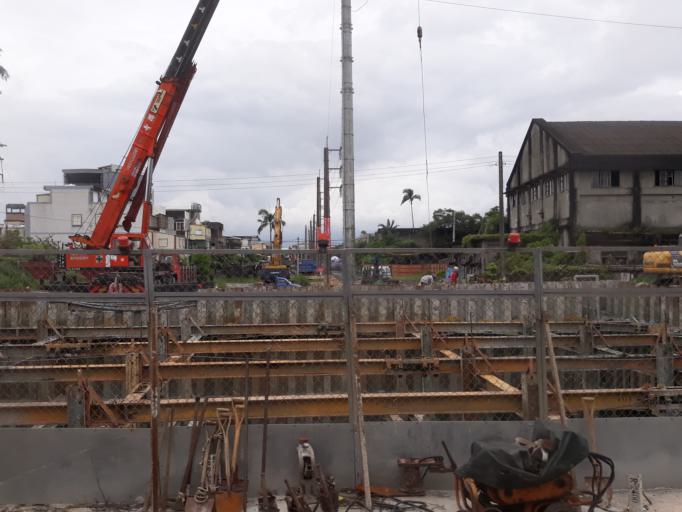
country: TW
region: Taiwan
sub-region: Yilan
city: Yilan
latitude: 24.6933
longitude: 121.7751
